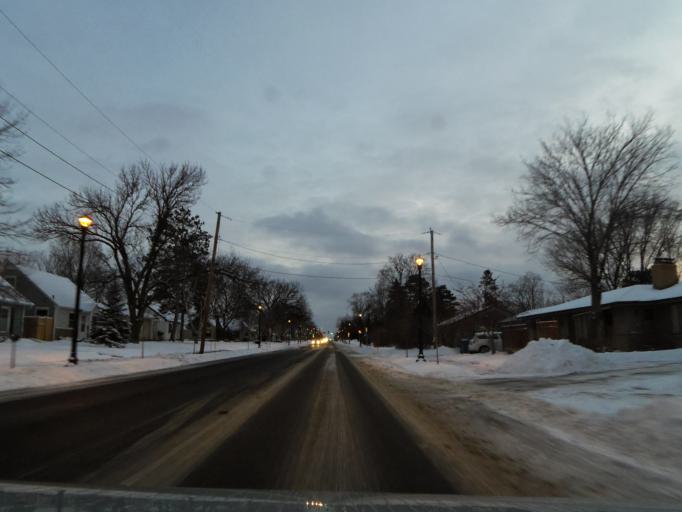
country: US
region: Minnesota
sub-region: Hennepin County
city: Richfield
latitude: 44.8977
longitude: -93.3087
